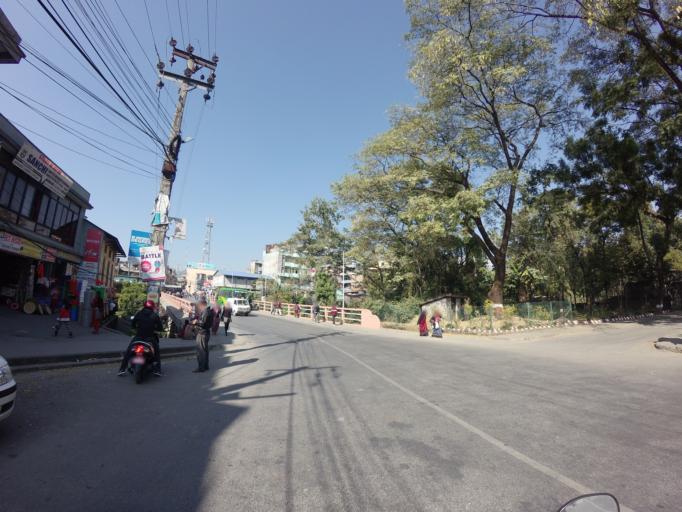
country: NP
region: Western Region
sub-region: Gandaki Zone
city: Pokhara
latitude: 28.2231
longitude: 83.9923
